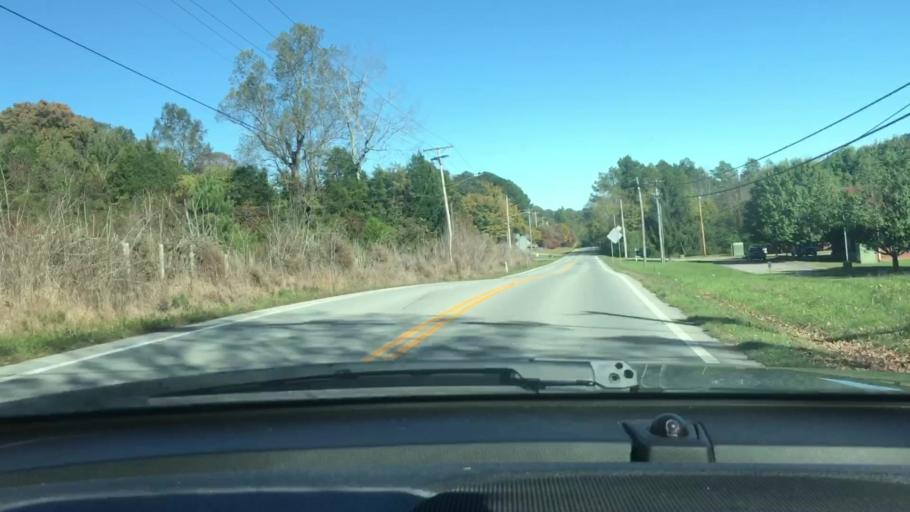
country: US
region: Tennessee
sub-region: Dickson County
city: Charlotte
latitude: 36.1787
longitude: -87.3364
